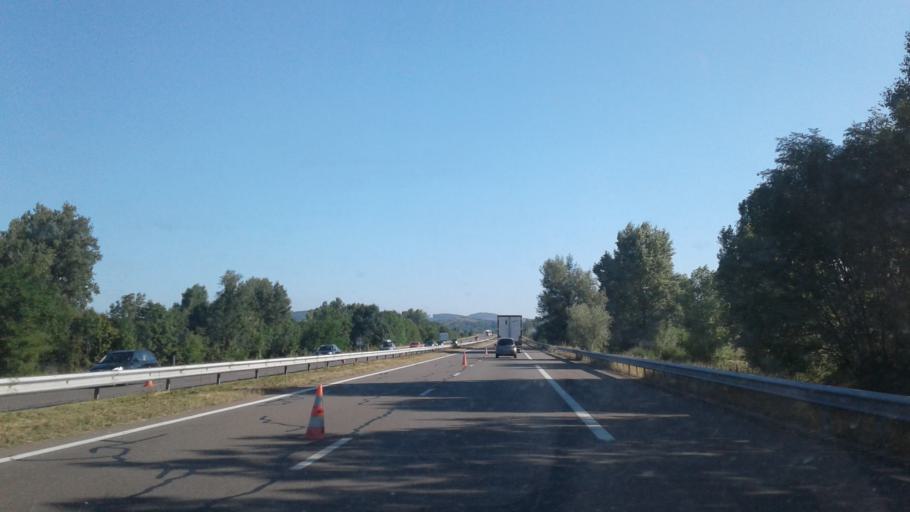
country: FR
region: Rhone-Alpes
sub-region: Departement de l'Ain
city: Saint-Martin-du-Mont
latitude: 46.0514
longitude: 5.3269
